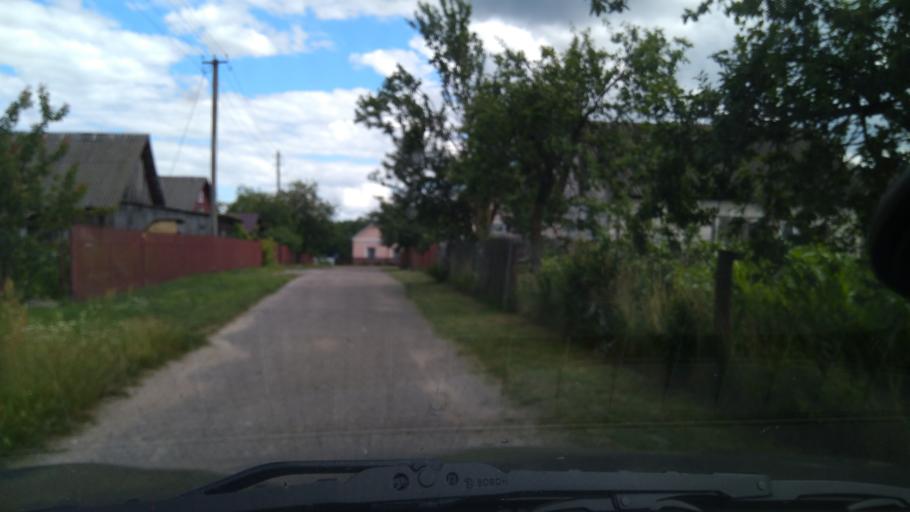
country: BY
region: Grodnenskaya
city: Masty
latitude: 53.4294
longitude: 24.6325
